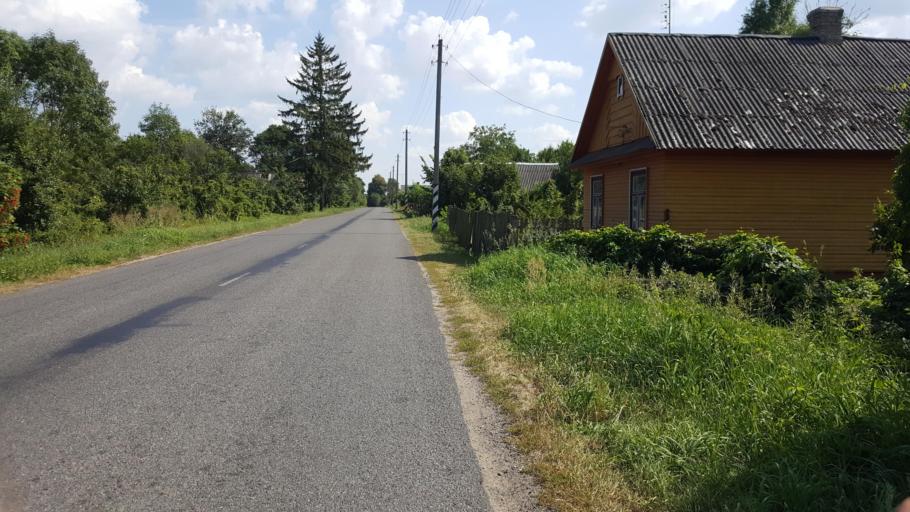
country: BY
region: Brest
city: Kamyanyuki
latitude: 52.5057
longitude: 23.6533
